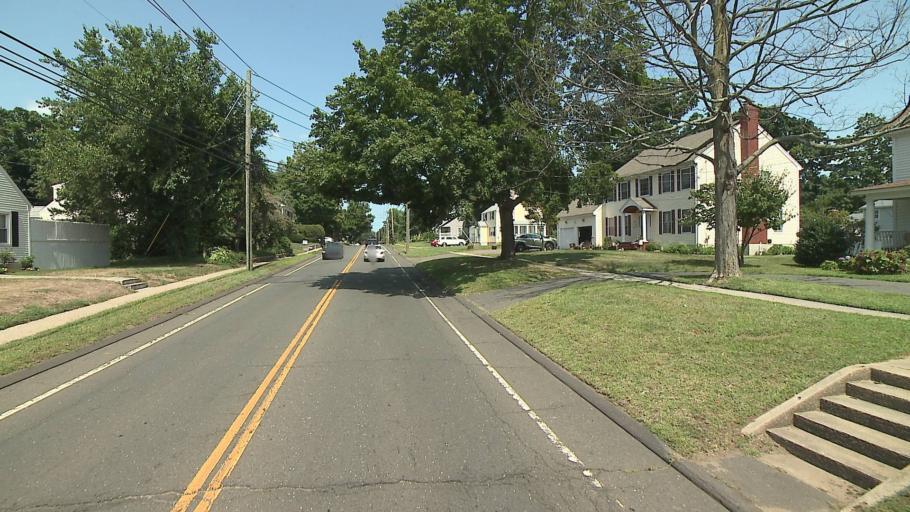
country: US
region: Connecticut
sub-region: Fairfield County
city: Stratford
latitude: 41.2113
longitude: -73.1193
